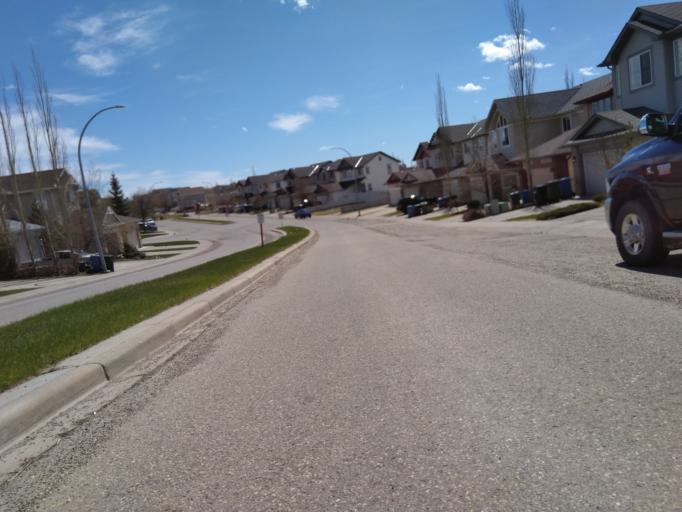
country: CA
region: Alberta
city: Calgary
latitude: 51.1327
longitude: -114.2467
